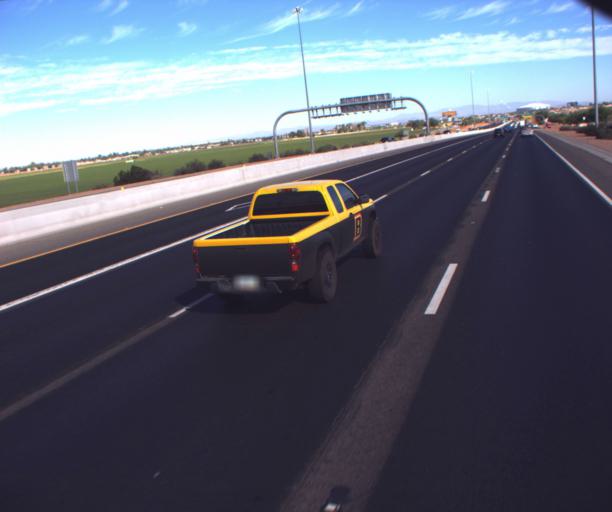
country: US
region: Arizona
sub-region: Maricopa County
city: Tolleson
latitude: 33.4812
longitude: -112.2637
